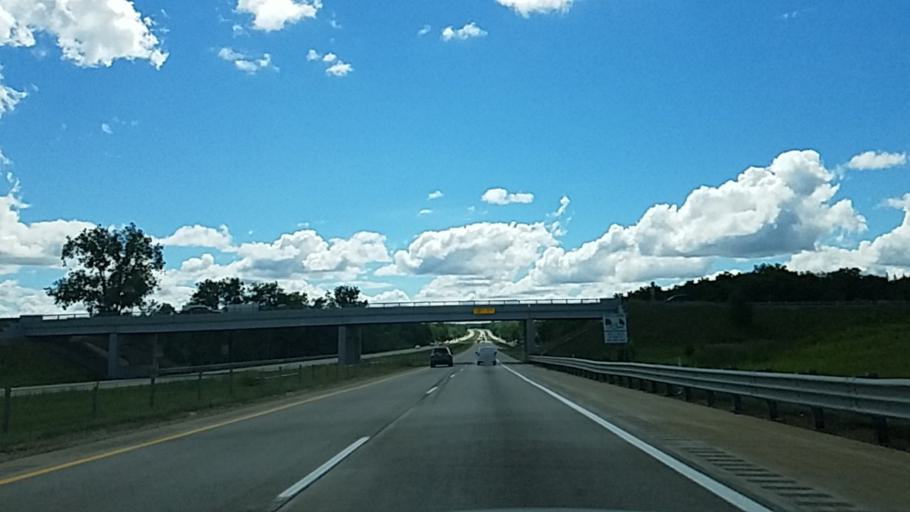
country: US
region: Michigan
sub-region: Genesee County
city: Linden
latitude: 42.7696
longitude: -83.7520
